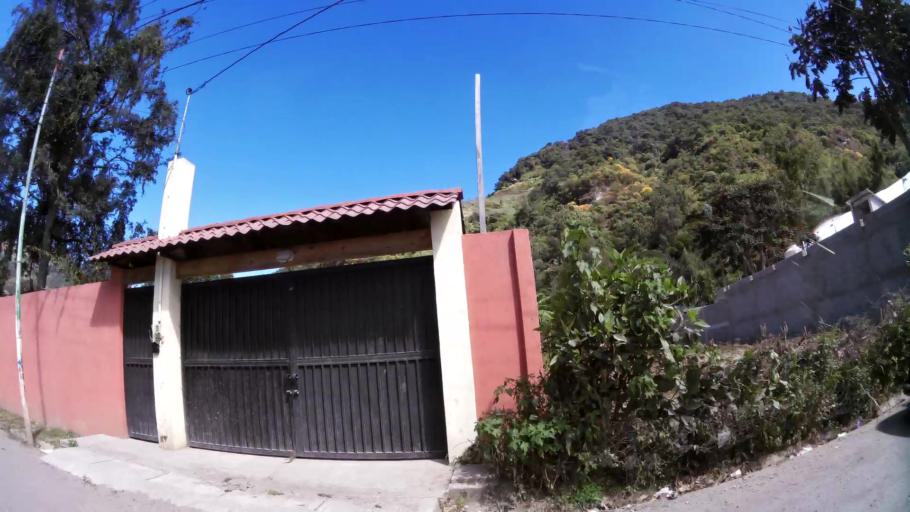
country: GT
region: Solola
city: Panajachel
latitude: 14.7385
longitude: -91.1504
